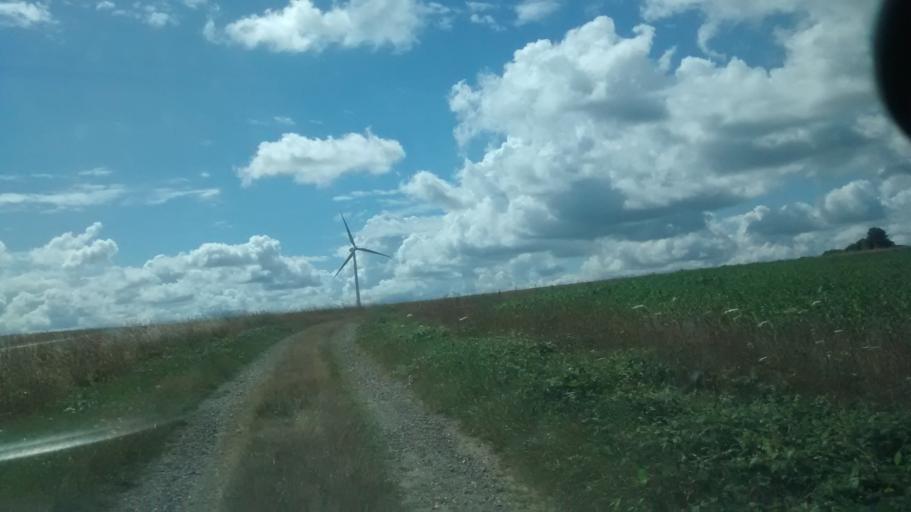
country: FR
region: Brittany
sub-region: Departement d'Ille-et-Vilaine
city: Grand-Fougeray
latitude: 47.7767
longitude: -1.7541
